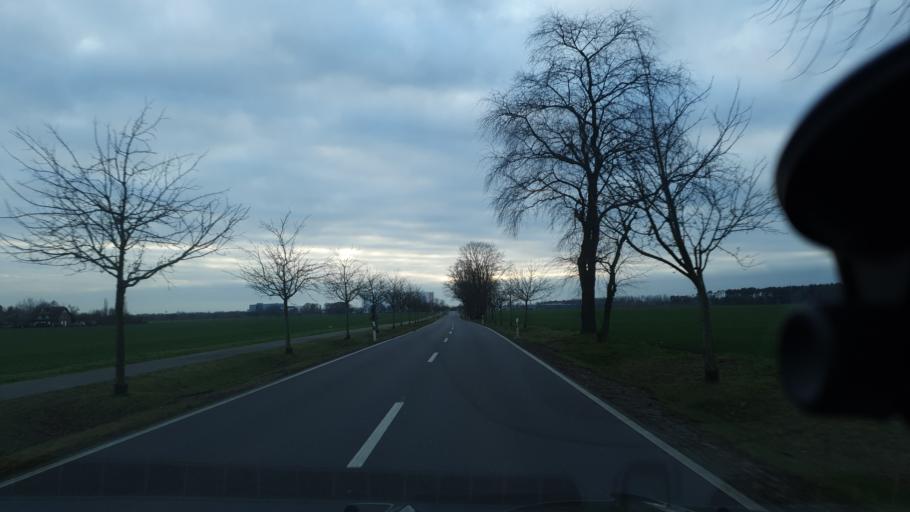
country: DE
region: Brandenburg
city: Schulzendorf
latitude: 52.3783
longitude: 13.5813
